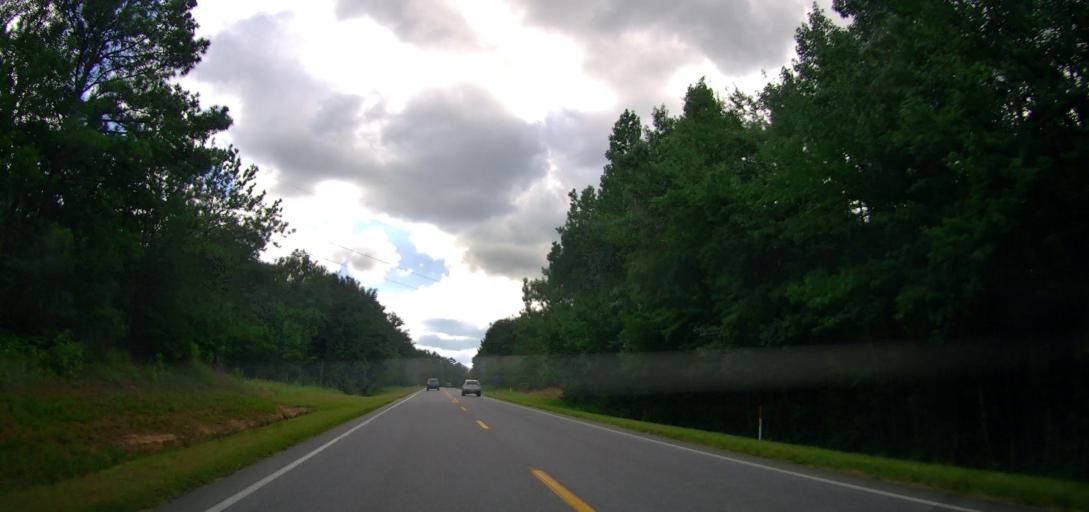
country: US
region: Alabama
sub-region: Russell County
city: Ladonia
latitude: 32.4516
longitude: -85.2147
